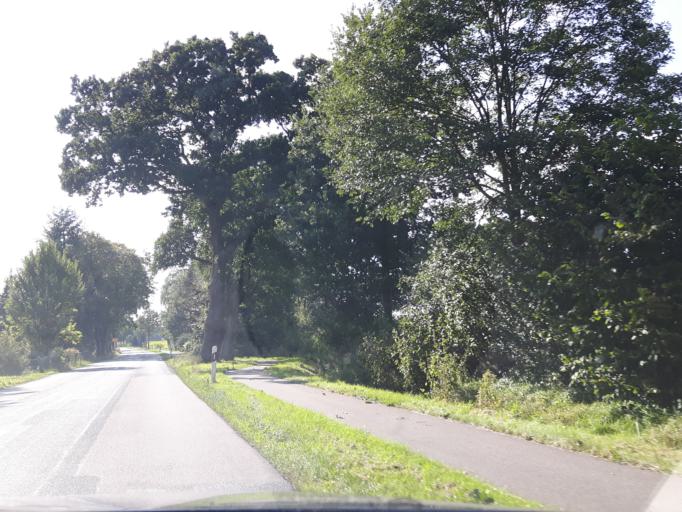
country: DE
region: Lower Saxony
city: Grossenkneten
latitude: 53.0043
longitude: 8.3067
